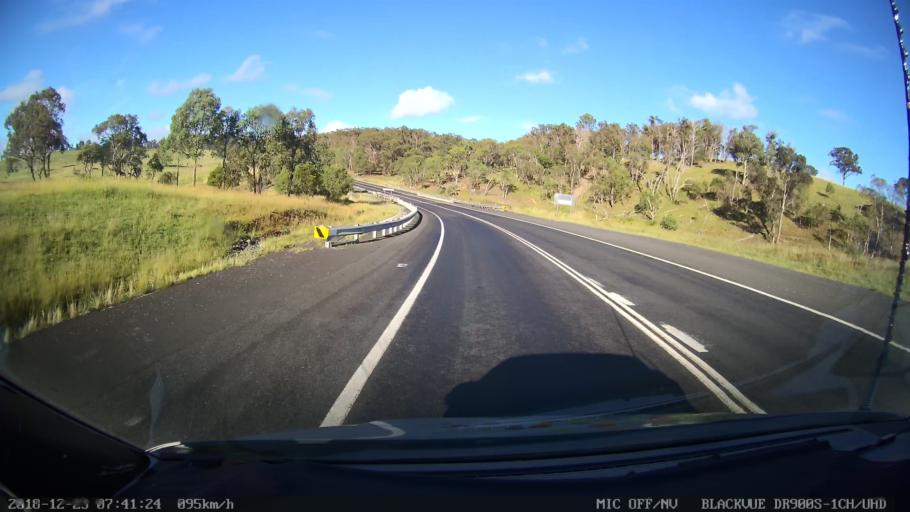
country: AU
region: New South Wales
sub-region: Armidale Dumaresq
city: Enmore
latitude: -30.5139
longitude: 151.9934
